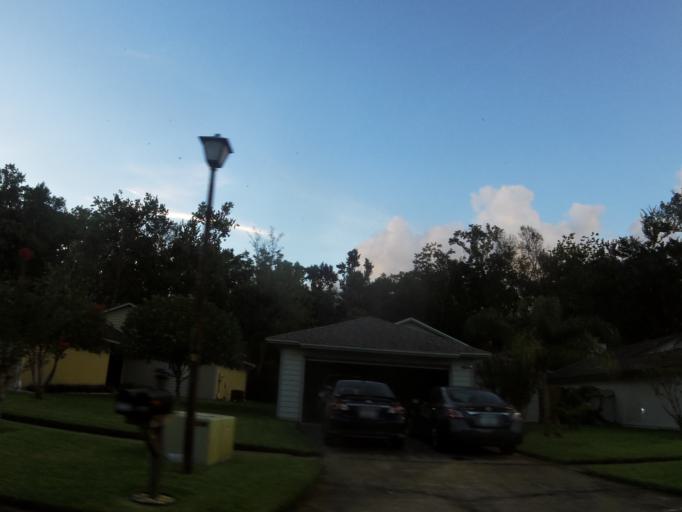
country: US
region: Florida
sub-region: Duval County
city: Jacksonville
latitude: 30.2301
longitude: -81.6032
